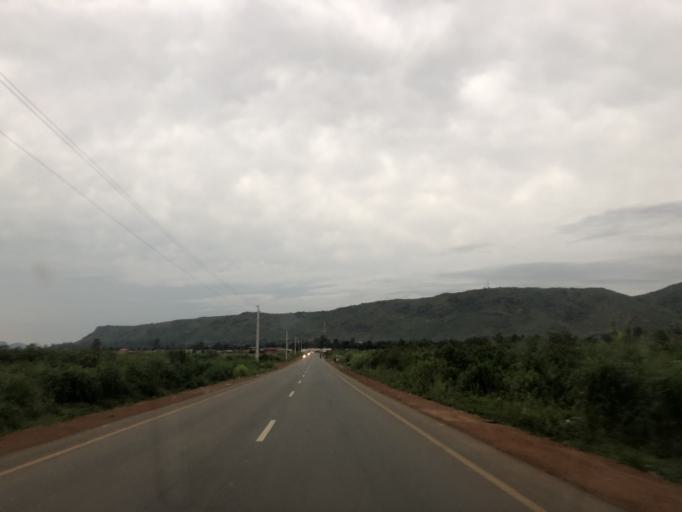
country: AO
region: Cuanza Sul
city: Uacu Cungo
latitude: -11.3415
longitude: 15.1036
